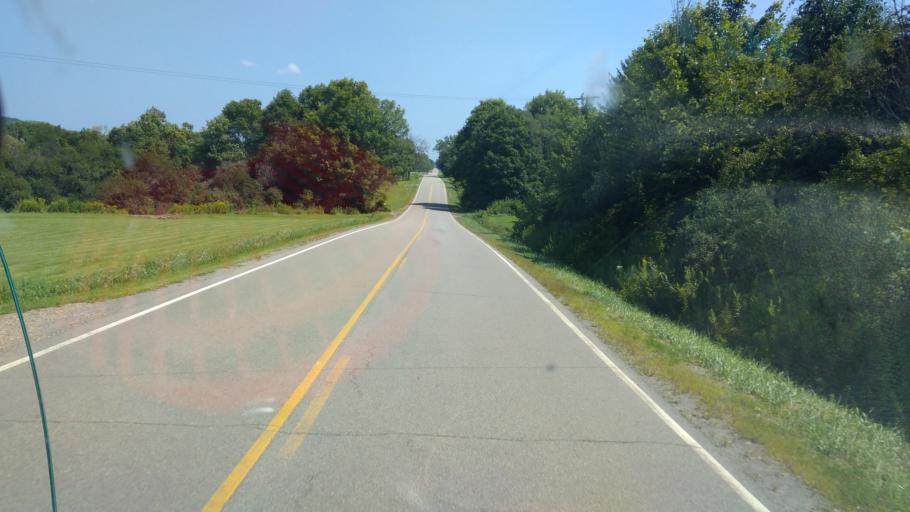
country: US
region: New York
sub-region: Allegany County
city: Belmont
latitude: 42.2905
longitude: -77.9297
